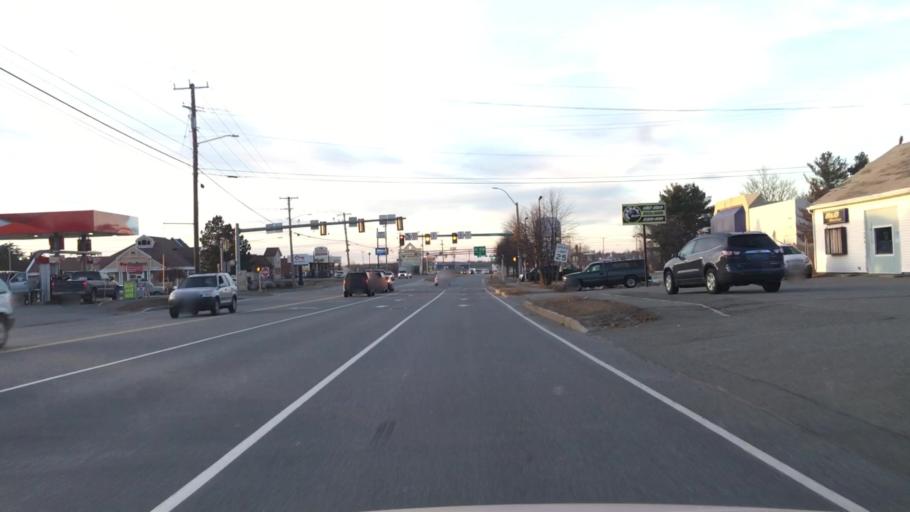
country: US
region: Maine
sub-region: Penobscot County
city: Brewer
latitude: 44.7833
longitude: -68.7493
